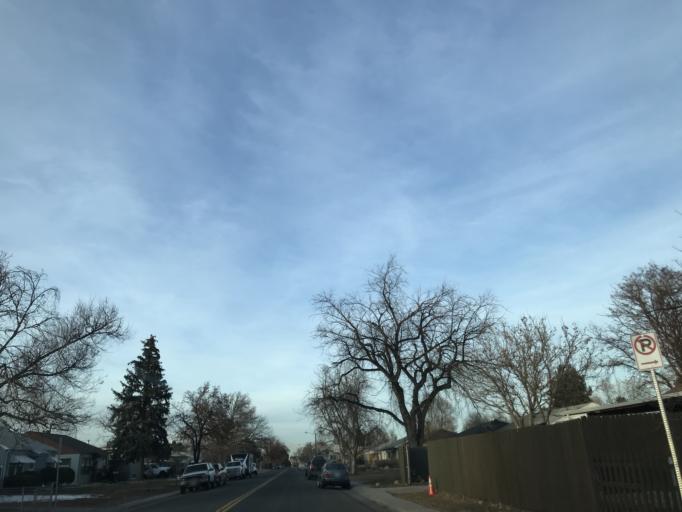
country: US
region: Colorado
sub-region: Adams County
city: Aurora
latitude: 39.7475
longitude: -104.8658
